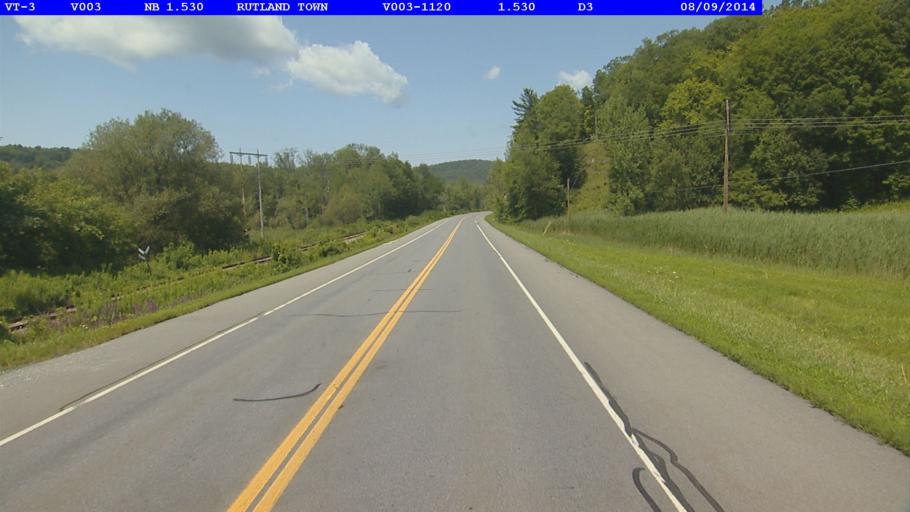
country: US
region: Vermont
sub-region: Rutland County
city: West Rutland
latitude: 43.6236
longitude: -73.0262
